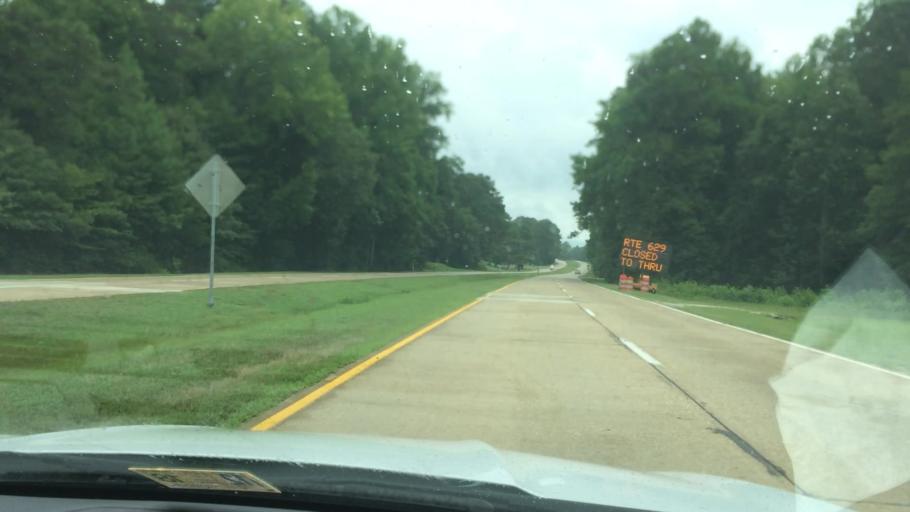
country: US
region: Virginia
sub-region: New Kent County
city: New Kent
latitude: 37.4410
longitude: -77.0334
